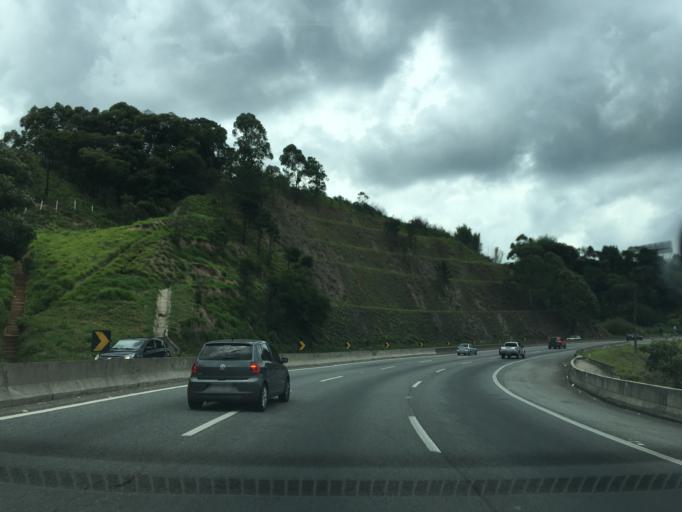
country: BR
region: Sao Paulo
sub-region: Mairipora
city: Mairipora
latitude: -23.2911
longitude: -46.5857
